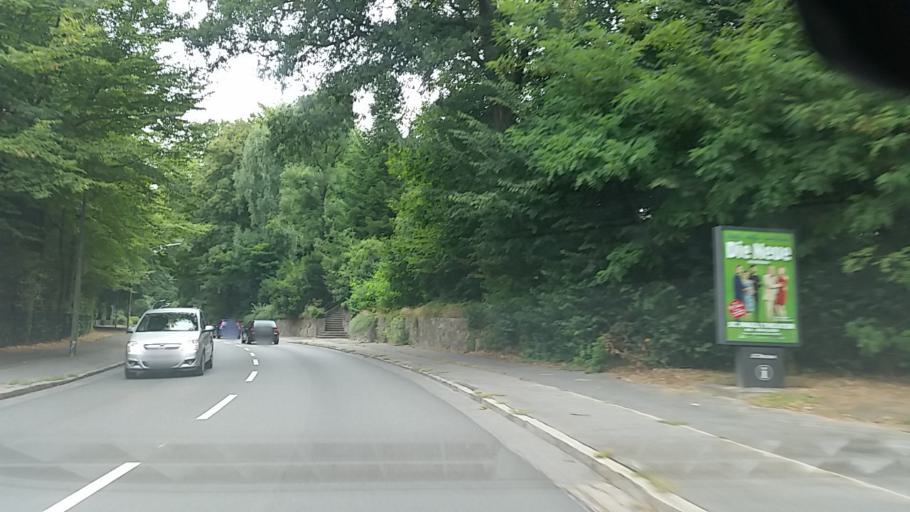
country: DE
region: Schleswig-Holstein
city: Reinbek
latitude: 53.5112
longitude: 10.2471
